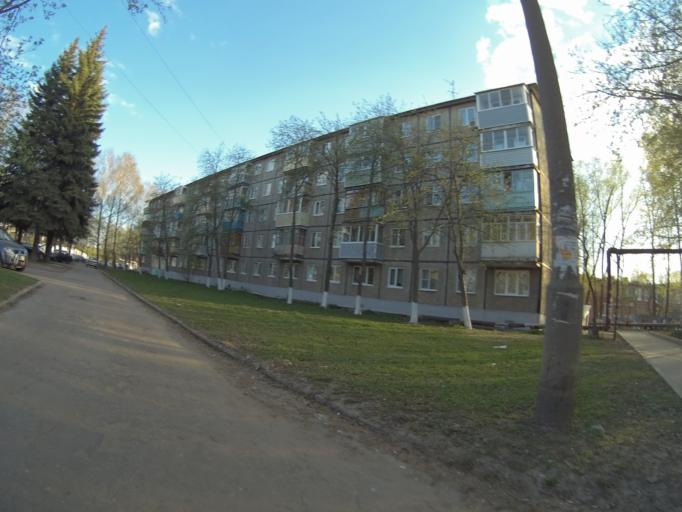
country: RU
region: Vladimir
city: Vladimir
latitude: 56.1444
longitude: 40.3681
